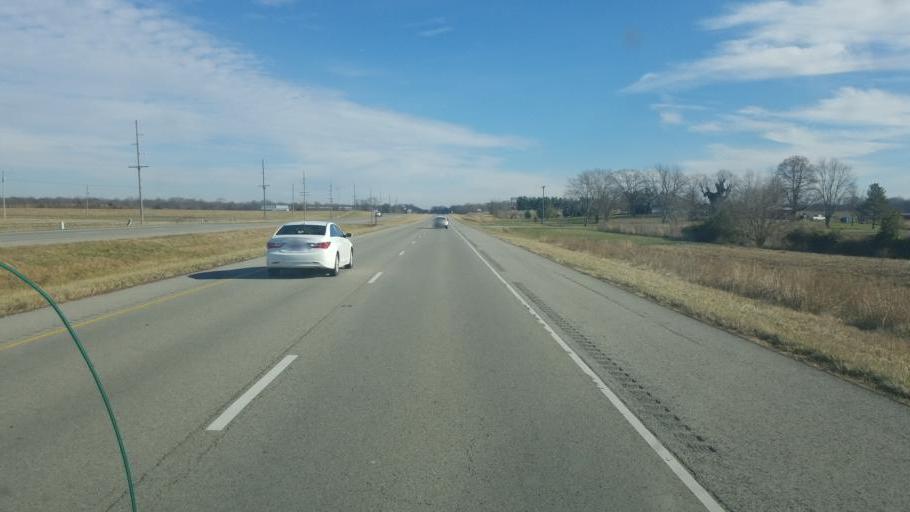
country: US
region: Illinois
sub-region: Williamson County
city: Marion
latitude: 37.7295
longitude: -88.8448
